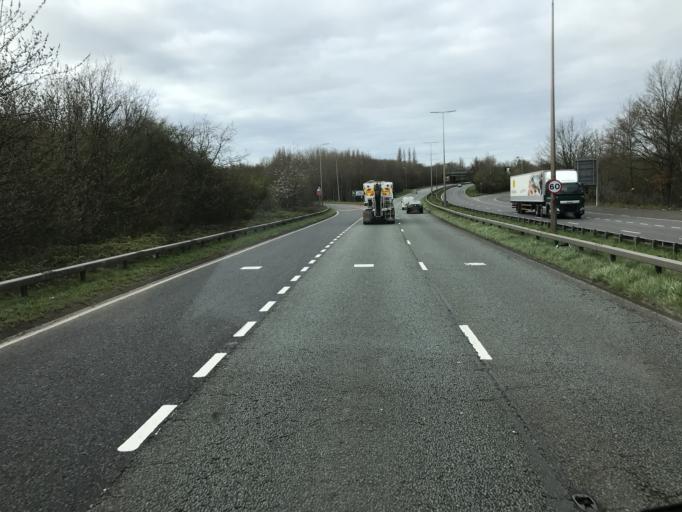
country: GB
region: England
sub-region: Borough of Halton
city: Hale
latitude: 53.3511
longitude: -2.8152
